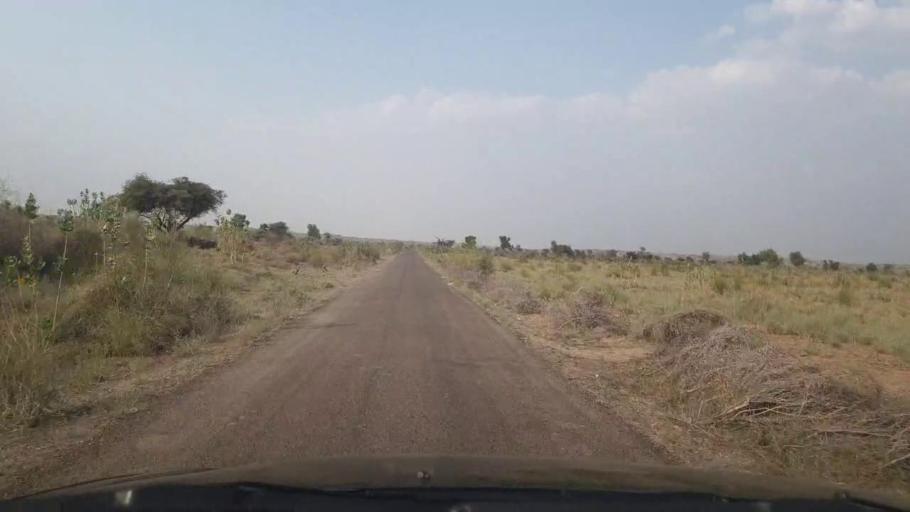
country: PK
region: Sindh
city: Islamkot
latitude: 25.0543
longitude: 70.5596
